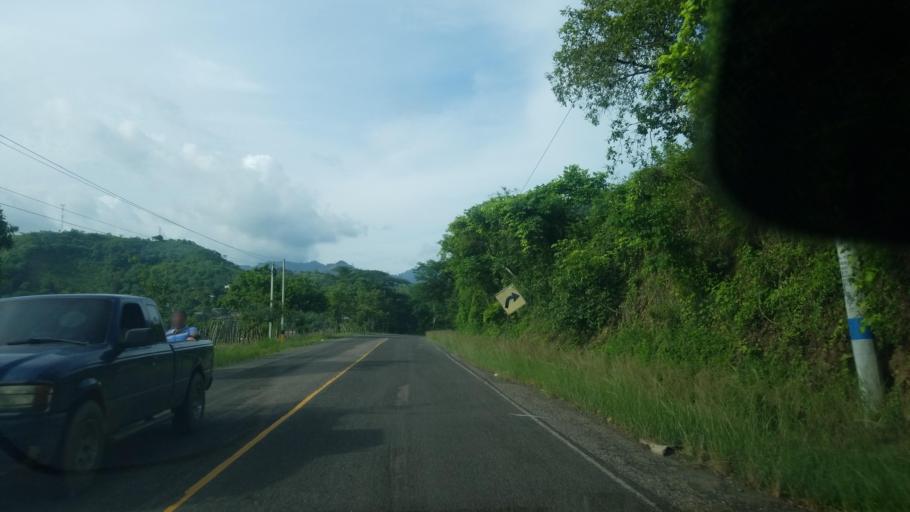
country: HN
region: Santa Barbara
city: Trinidad
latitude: 15.1394
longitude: -88.2413
